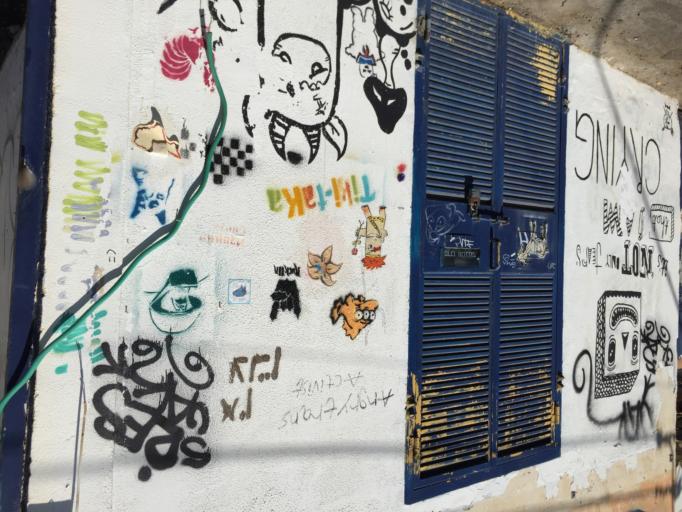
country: IL
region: Tel Aviv
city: Yafo
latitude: 32.0575
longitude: 34.7671
